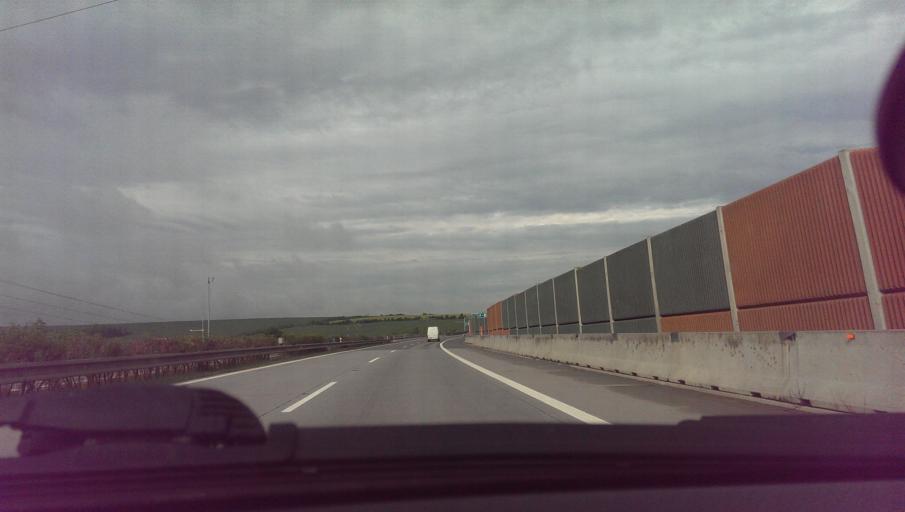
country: CZ
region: South Moravian
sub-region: Okres Vyskov
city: Vyskov
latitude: 49.2742
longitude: 17.0455
